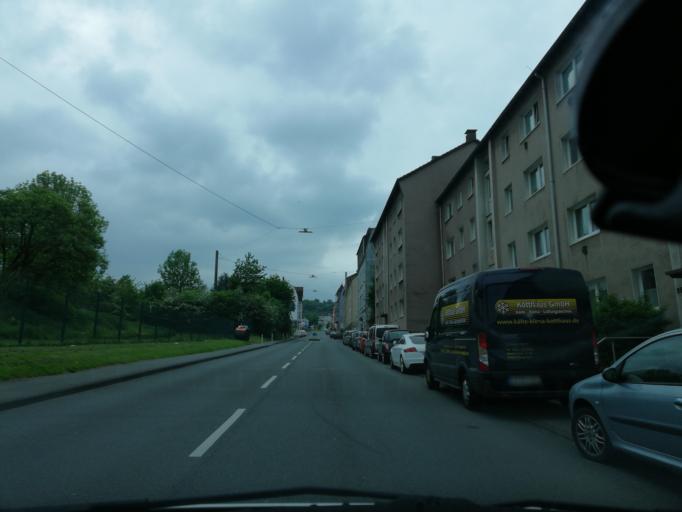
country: DE
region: North Rhine-Westphalia
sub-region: Regierungsbezirk Arnsberg
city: Schwelm
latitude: 51.2799
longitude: 7.2556
